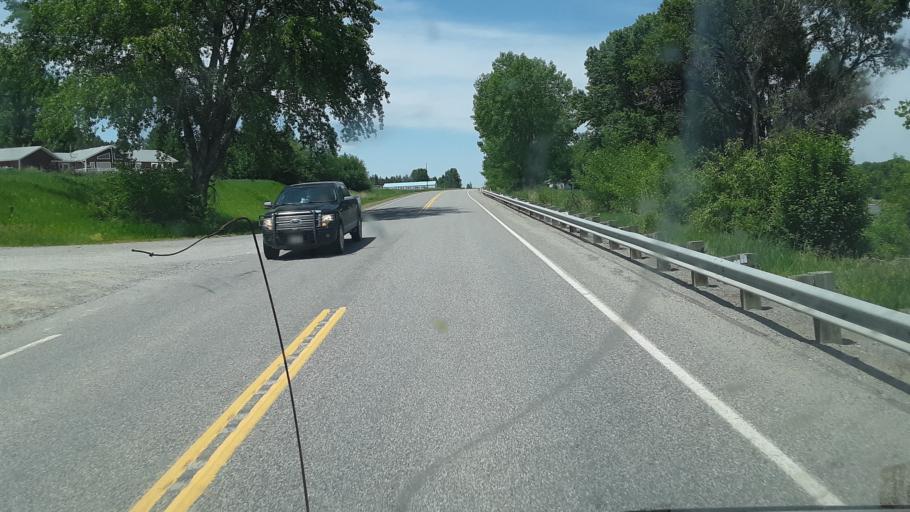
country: US
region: Montana
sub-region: Stillwater County
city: Columbus
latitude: 45.6216
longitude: -109.2426
